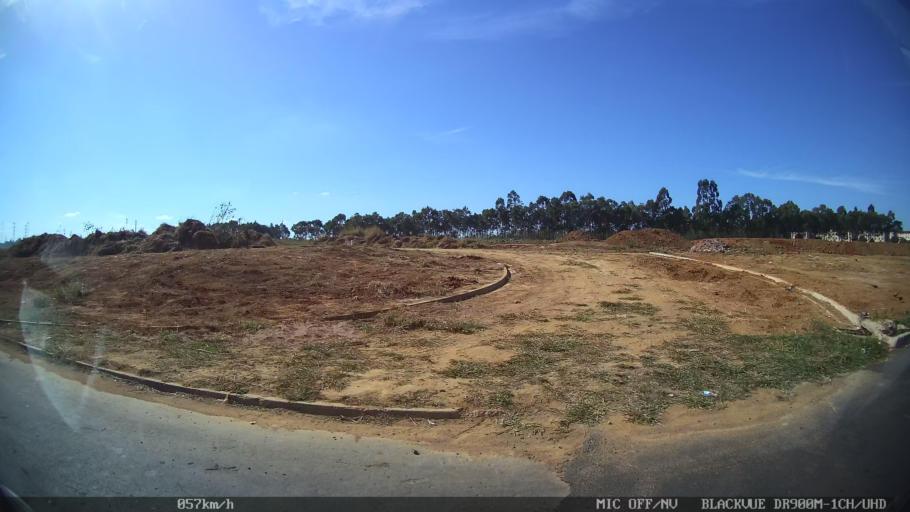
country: BR
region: Sao Paulo
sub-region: Franca
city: Franca
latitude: -20.4805
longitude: -47.4062
